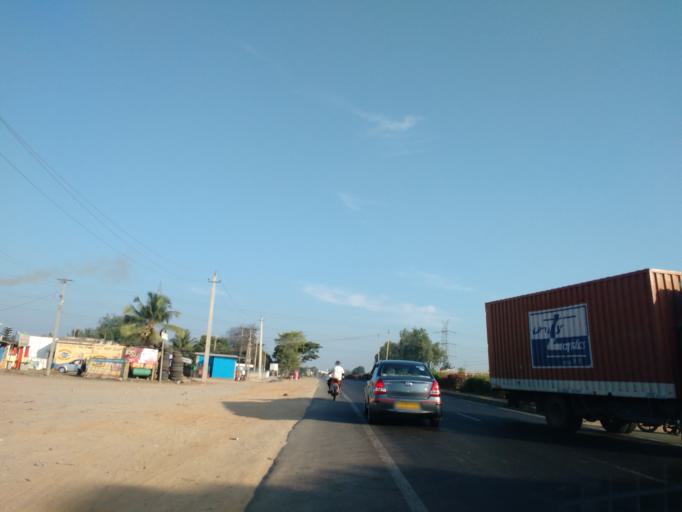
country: IN
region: Karnataka
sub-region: Bangalore Rural
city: Nelamangala
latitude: 13.1311
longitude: 77.3588
